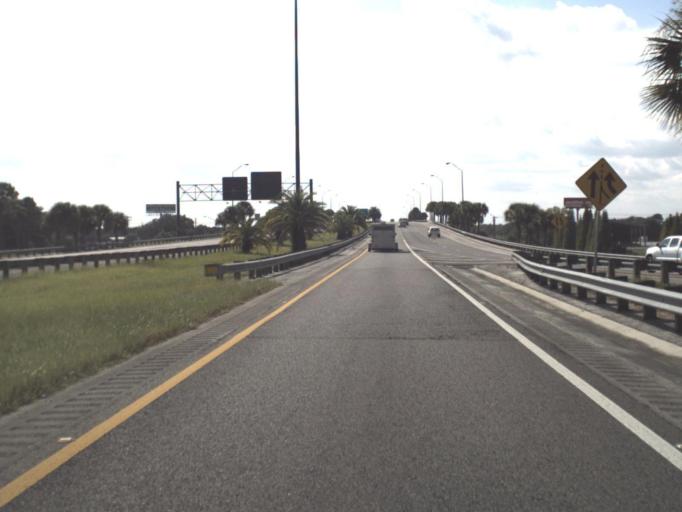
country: US
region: Florida
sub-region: Polk County
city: Winston
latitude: 28.0342
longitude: -82.0402
